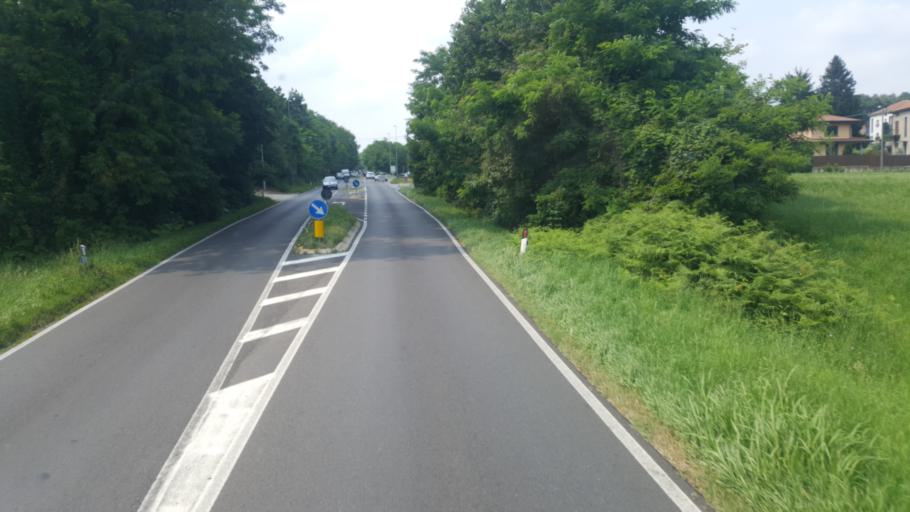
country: IT
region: Lombardy
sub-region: Provincia di Como
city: Oltrona di San Mamette
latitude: 45.7564
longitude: 8.9676
